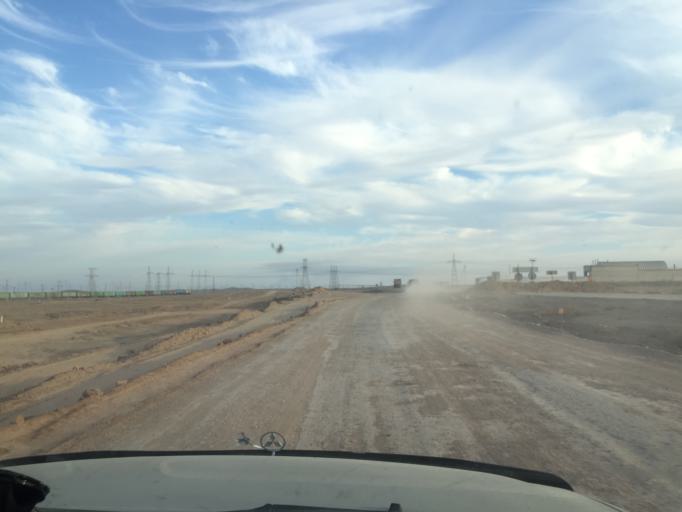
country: KZ
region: Almaty Oblysy
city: Ulken
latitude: 45.1943
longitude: 73.9082
